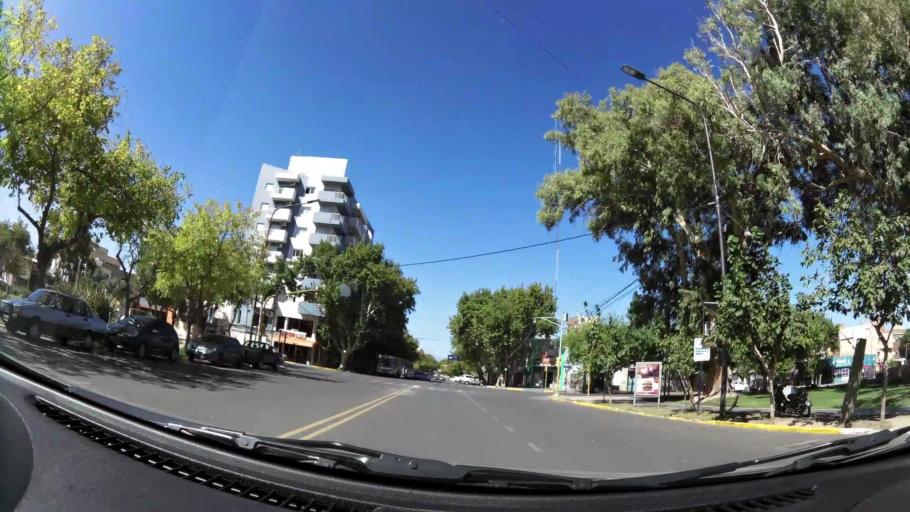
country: AR
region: San Juan
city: San Juan
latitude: -31.5381
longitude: -68.5368
